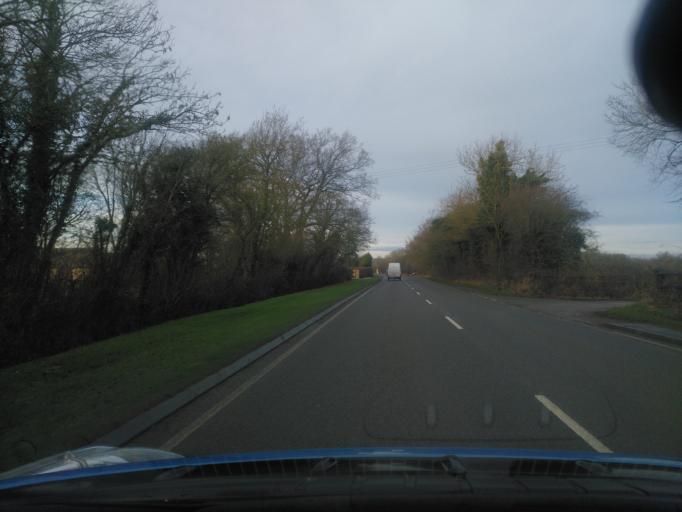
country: GB
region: England
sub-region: Gloucestershire
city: Moreton in Marsh
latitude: 51.9840
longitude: -1.6573
